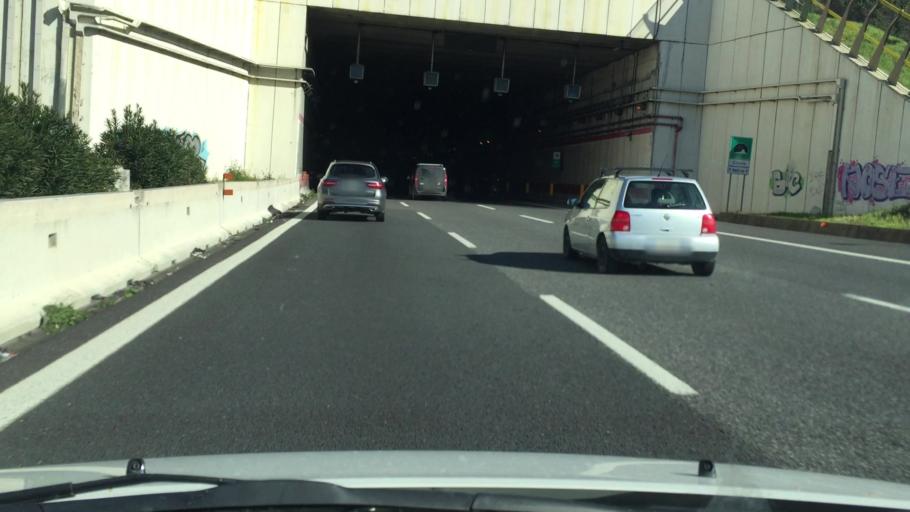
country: VA
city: Vatican City
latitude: 41.9744
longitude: 12.4221
